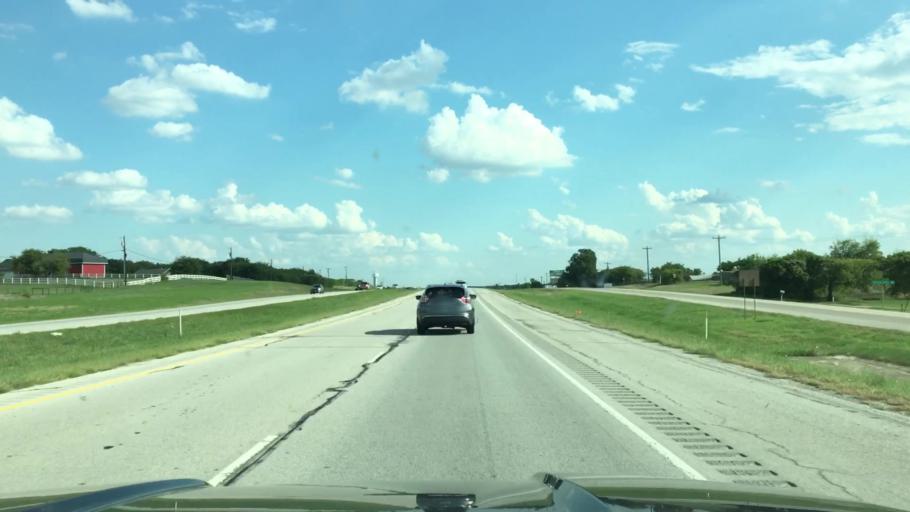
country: US
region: Texas
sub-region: Tarrant County
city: Pecan Acres
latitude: 32.9885
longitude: -97.4294
